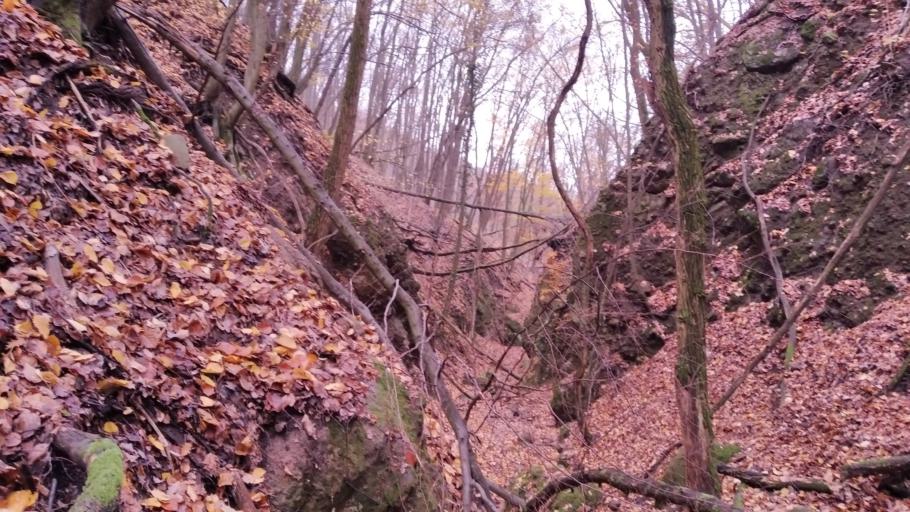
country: HU
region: Pest
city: Csobanka
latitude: 47.6811
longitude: 18.9560
